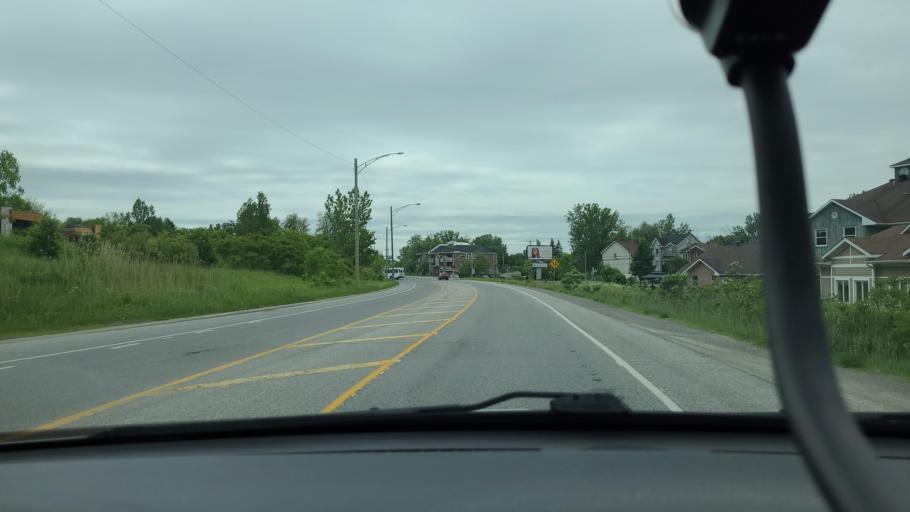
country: CA
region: Quebec
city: Bois-des-Filion
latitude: 45.6545
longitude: -73.7474
